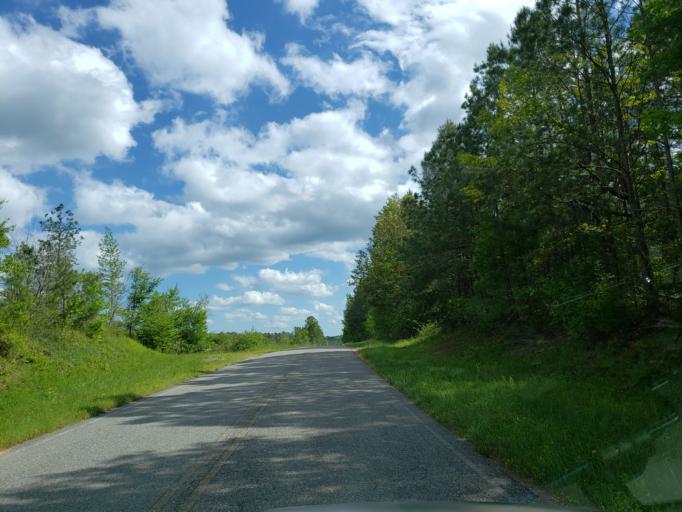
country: US
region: Georgia
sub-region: Haralson County
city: Tallapoosa
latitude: 33.7062
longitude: -85.3800
